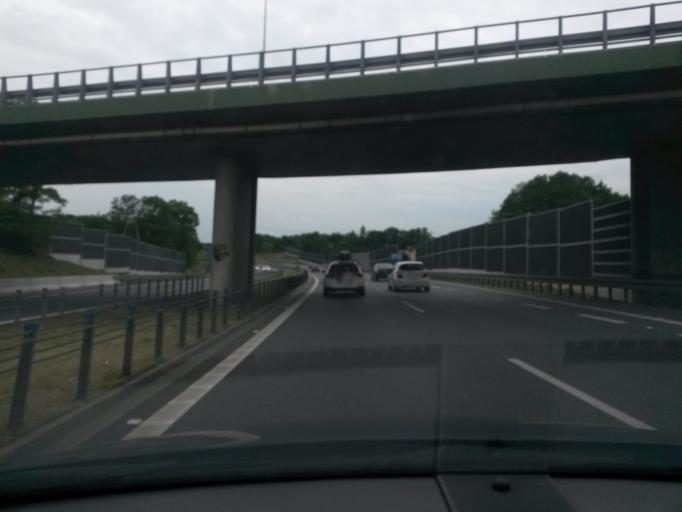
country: PL
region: Masovian Voivodeship
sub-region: Powiat zyrardowski
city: Mszczonow
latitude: 51.9769
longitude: 20.5061
